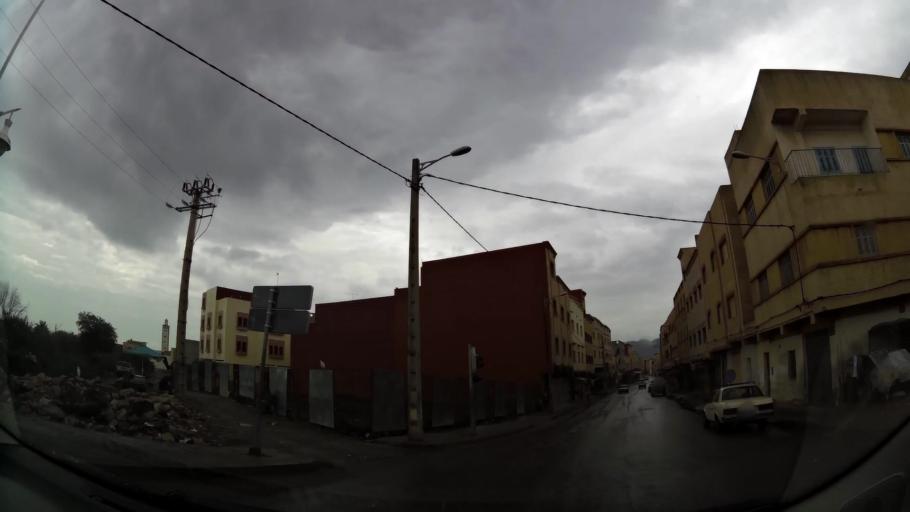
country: MA
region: Oriental
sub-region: Nador
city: Nador
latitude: 35.1539
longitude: -2.9804
